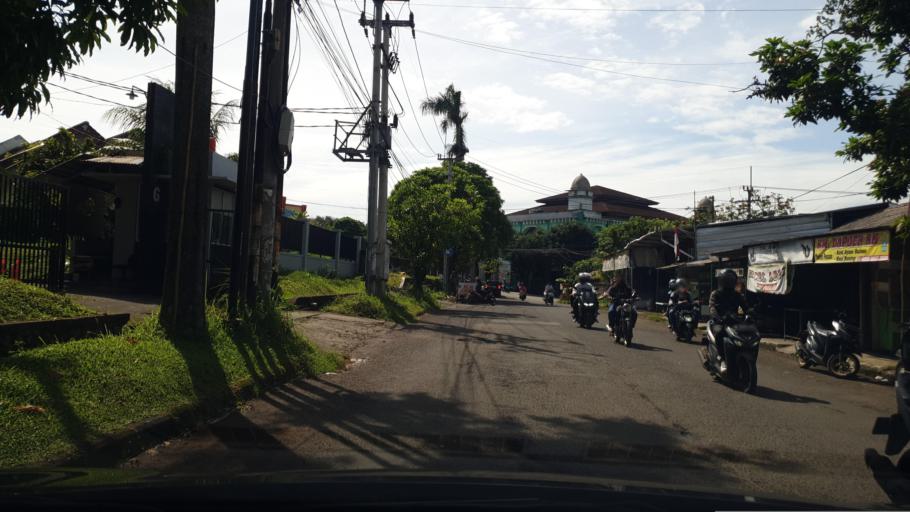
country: ID
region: West Java
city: Sawangan
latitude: -6.4059
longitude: 106.7743
